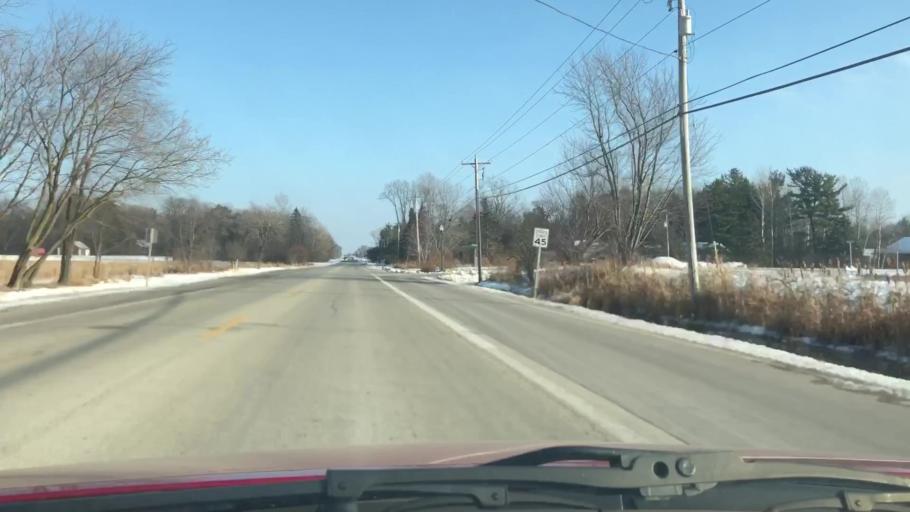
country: US
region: Wisconsin
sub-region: Outagamie County
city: Appleton
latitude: 44.3166
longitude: -88.4241
